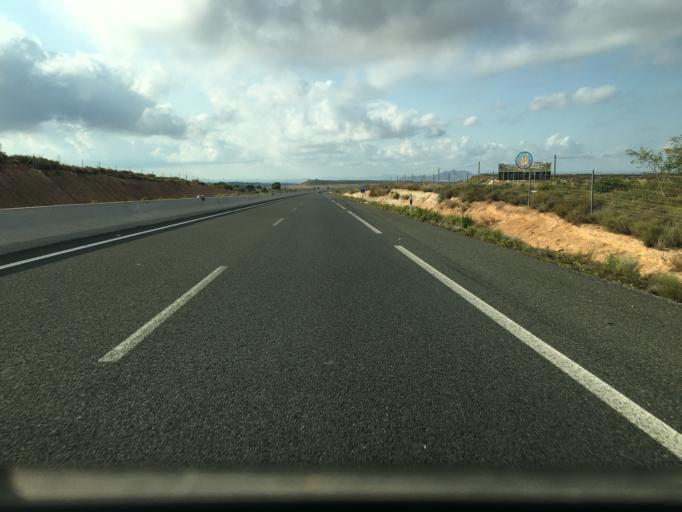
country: ES
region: Murcia
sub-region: Murcia
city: Beniel
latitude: 37.9136
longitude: -0.9599
